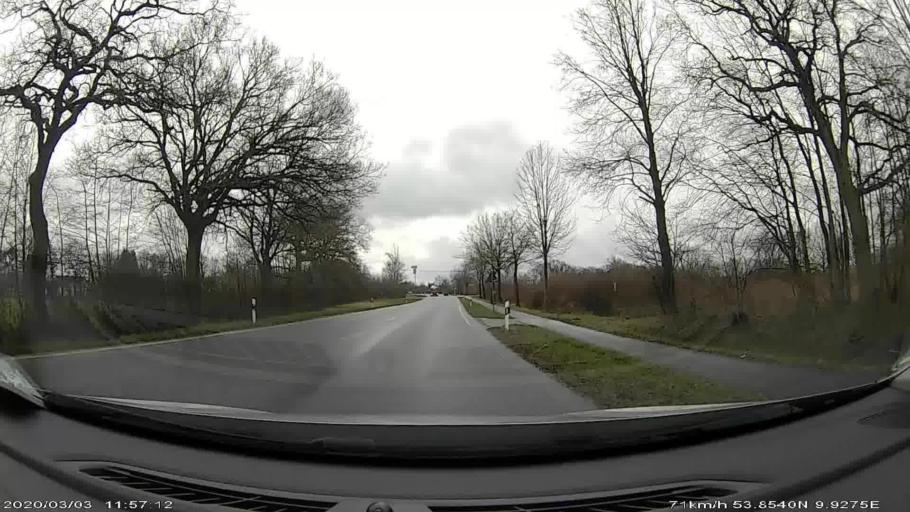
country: DE
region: Schleswig-Holstein
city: Nutzen
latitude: 53.8521
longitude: 9.9294
